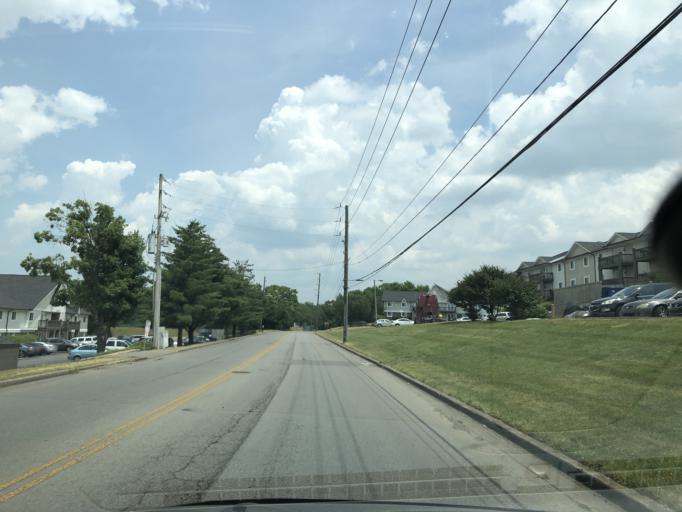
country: US
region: Tennessee
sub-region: Davidson County
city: Oak Hill
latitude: 36.0670
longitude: -86.6907
